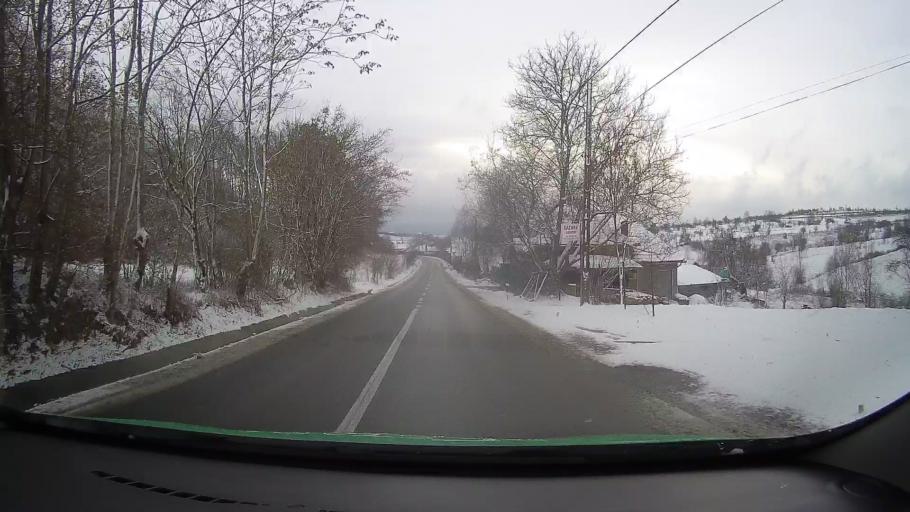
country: RO
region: Hunedoara
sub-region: Oras Hateg
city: Hateg
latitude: 45.6283
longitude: 22.9317
